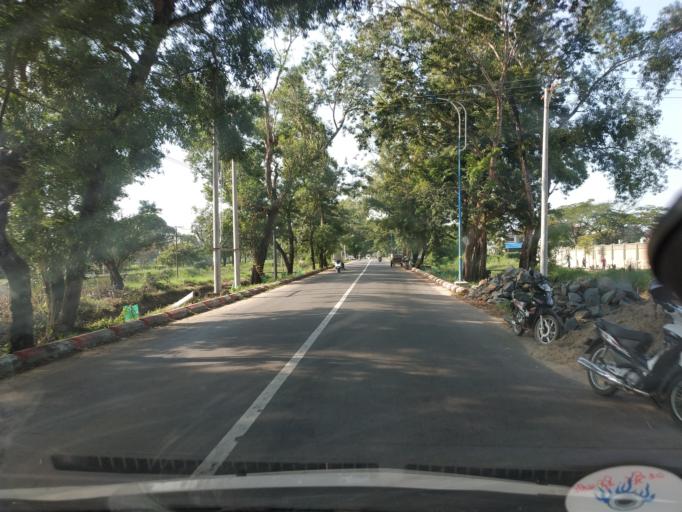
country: MM
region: Ayeyarwady
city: Pathein
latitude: 16.8091
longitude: 94.7559
